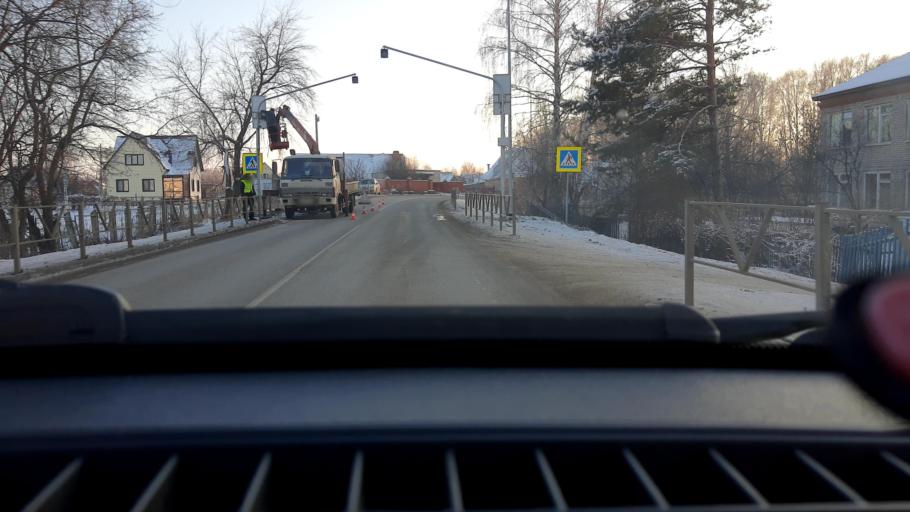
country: RU
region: Bashkortostan
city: Iglino
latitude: 54.8262
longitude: 56.3938
